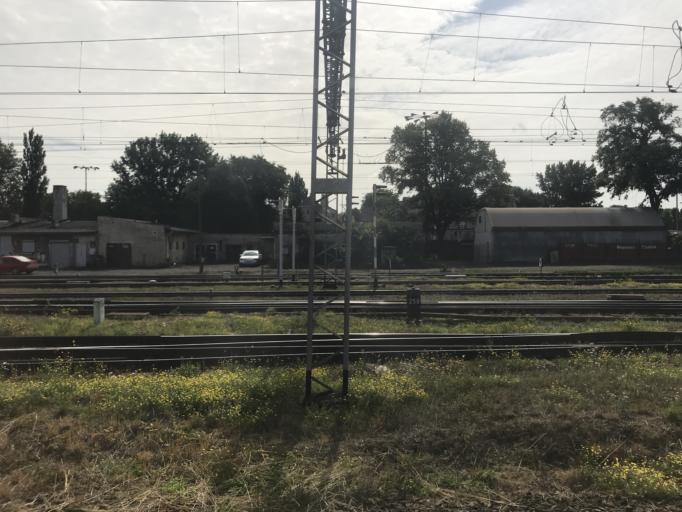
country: PL
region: Kujawsko-Pomorskie
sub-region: Powiat inowroclawski
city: Inowroclaw
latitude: 52.8035
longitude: 18.2424
